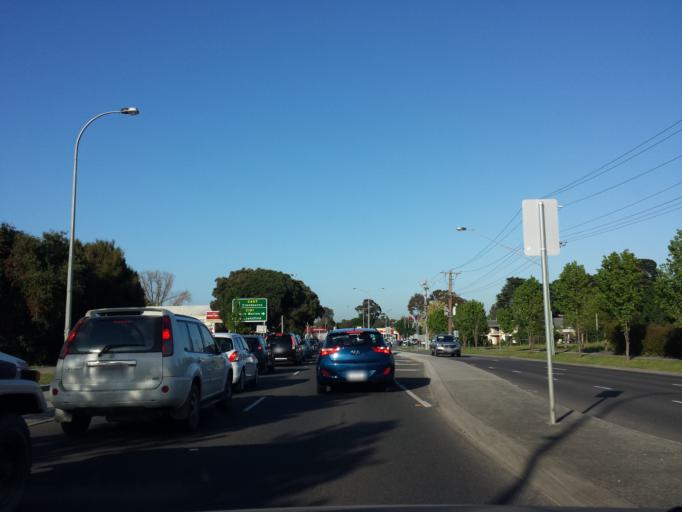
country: AU
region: Victoria
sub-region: Casey
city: Berwick
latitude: -38.0298
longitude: 145.3458
